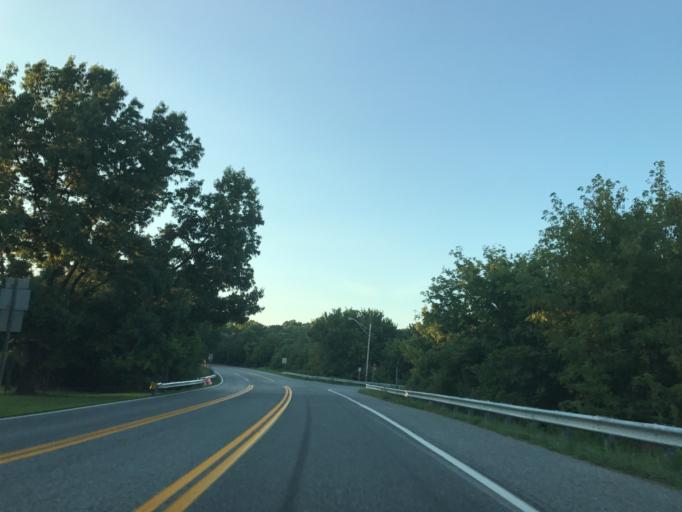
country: US
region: Maryland
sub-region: Harford County
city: Jarrettsville
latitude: 39.5892
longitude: -76.5093
